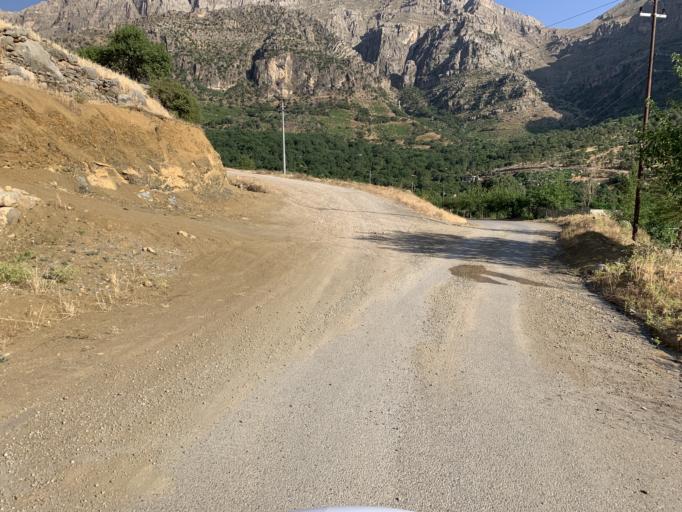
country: IQ
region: As Sulaymaniyah
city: Qeladize
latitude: 35.9913
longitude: 45.1995
